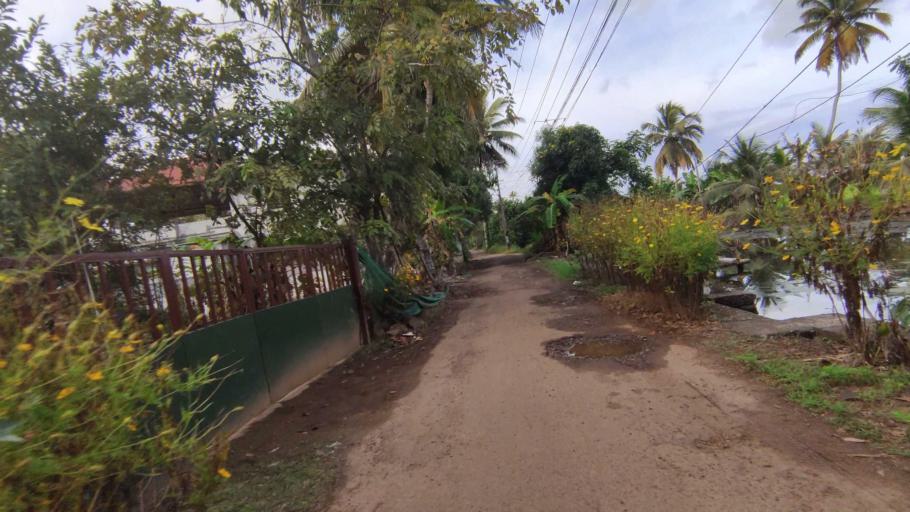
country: IN
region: Kerala
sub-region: Kottayam
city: Kottayam
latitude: 9.5985
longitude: 76.4397
